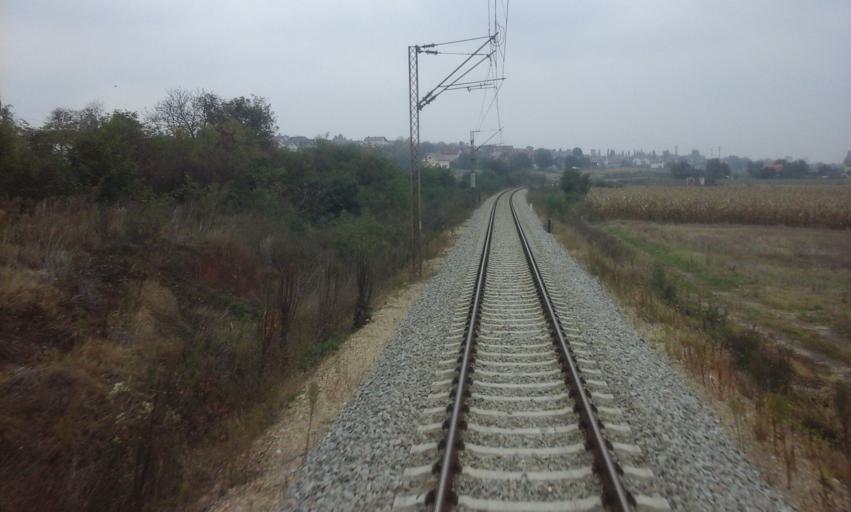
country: RS
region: Central Serbia
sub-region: Belgrade
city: Mladenovac
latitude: 44.4582
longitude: 20.6713
